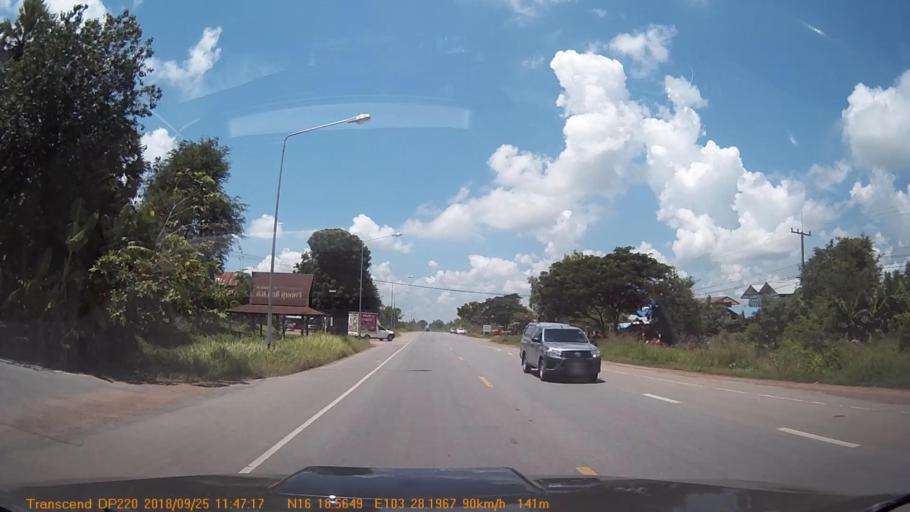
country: TH
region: Kalasin
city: Khong Chai
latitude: 16.3094
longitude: 103.4700
